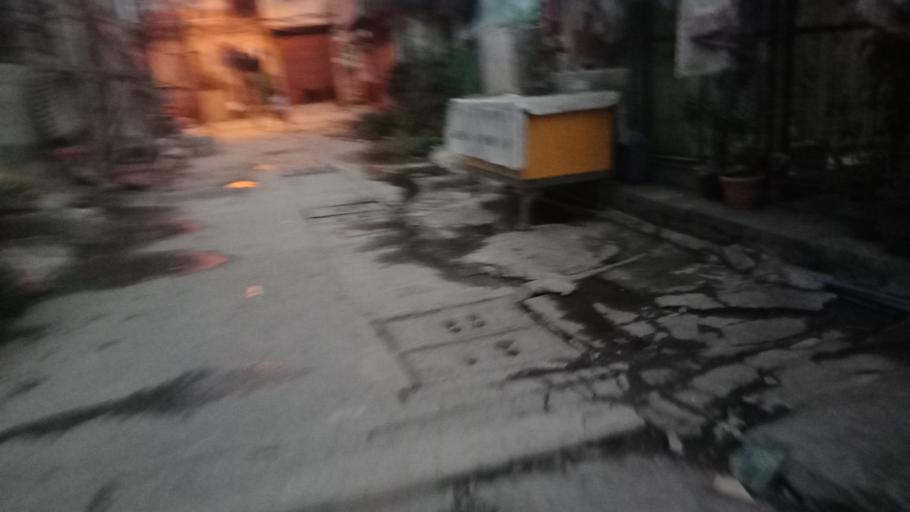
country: PH
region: Calabarzon
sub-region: Province of Rizal
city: Taguig
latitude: 14.5435
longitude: 121.1027
